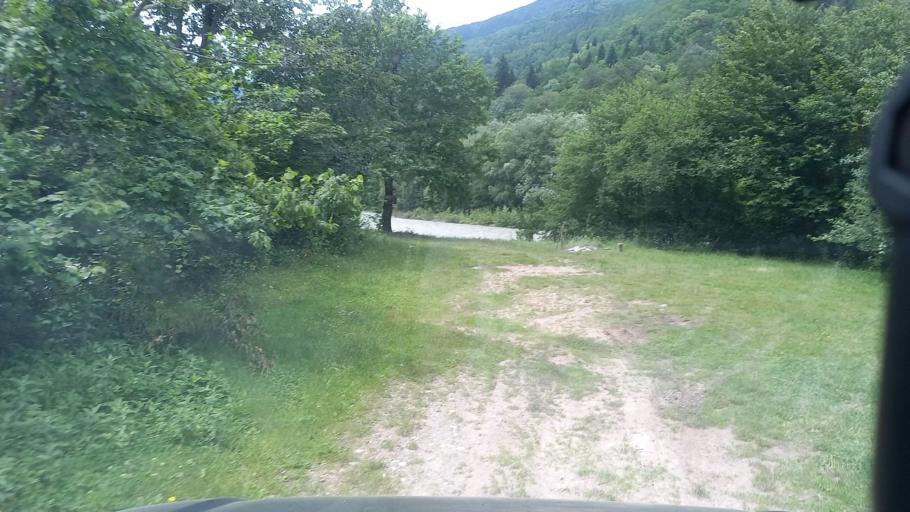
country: RU
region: Karachayevo-Cherkesiya
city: Kurdzhinovo
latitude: 43.8306
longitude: 40.9228
